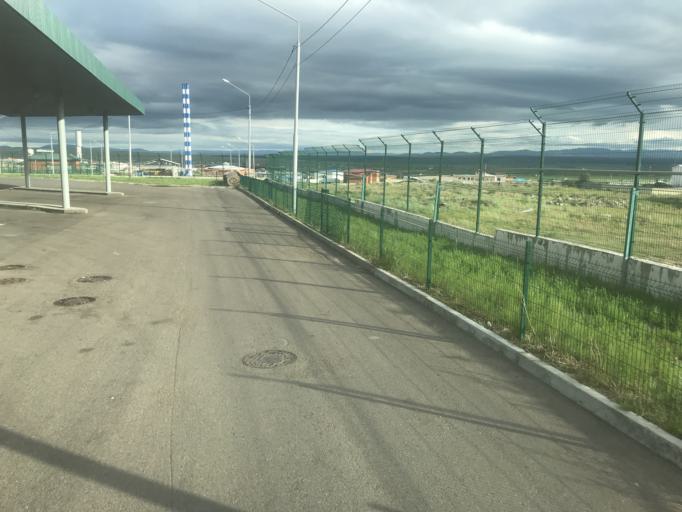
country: MN
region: Selenge
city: Altanbulag
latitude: 50.3258
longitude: 106.4858
